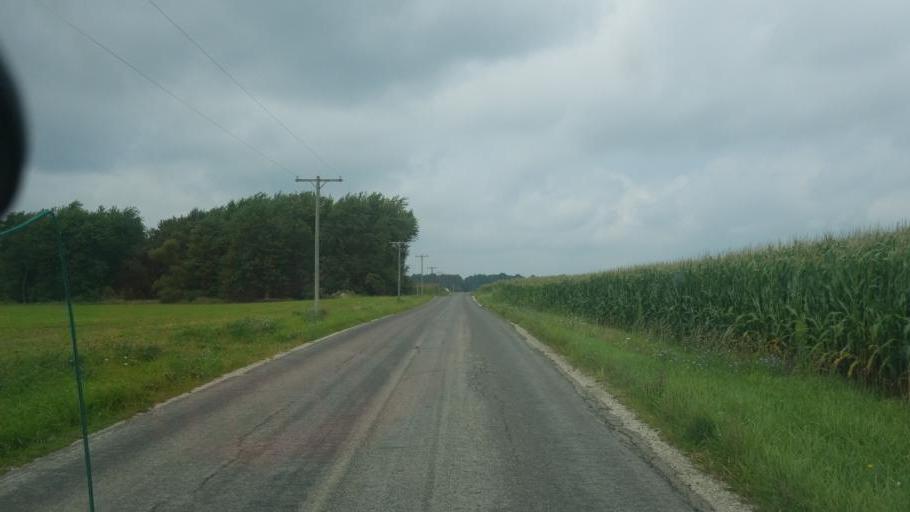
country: US
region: Ohio
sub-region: Huron County
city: Greenwich
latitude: 40.9600
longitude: -82.4625
